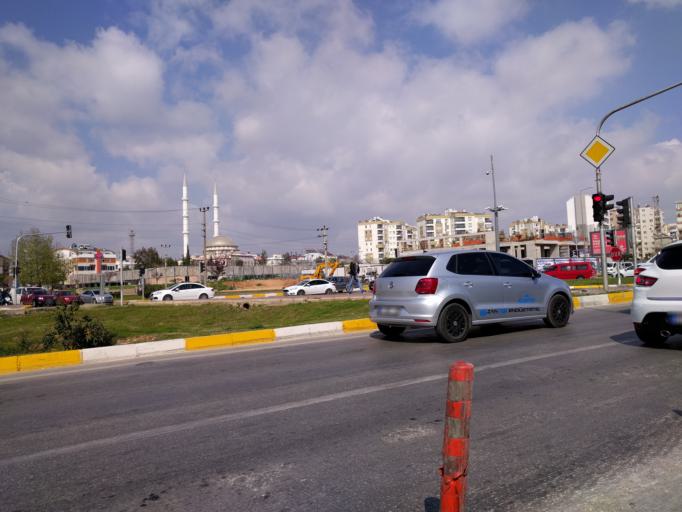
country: TR
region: Antalya
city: Antalya
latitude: 36.9005
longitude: 30.6521
